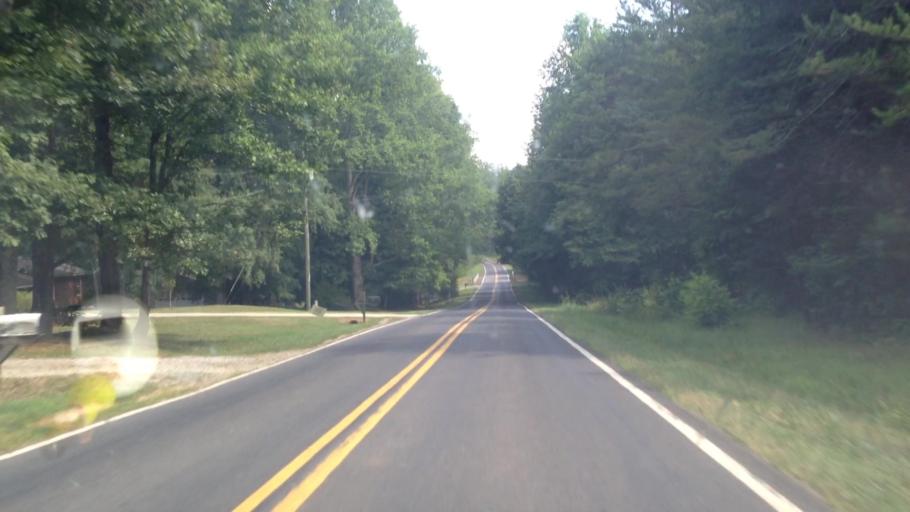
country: US
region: North Carolina
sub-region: Forsyth County
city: Walkertown
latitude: 36.2165
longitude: -80.1140
